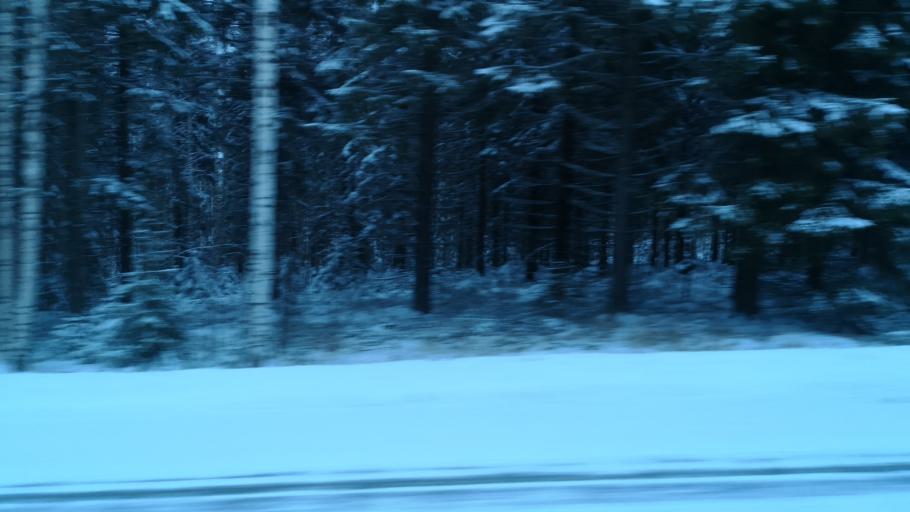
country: FI
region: Southern Savonia
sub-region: Savonlinna
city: Savonlinna
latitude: 61.8931
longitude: 28.9246
